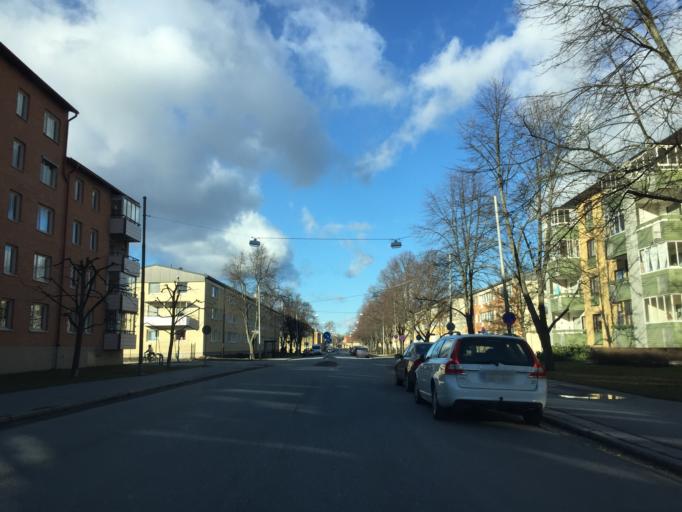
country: SE
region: OErebro
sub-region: Orebro Kommun
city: Orebro
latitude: 59.2805
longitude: 15.2103
